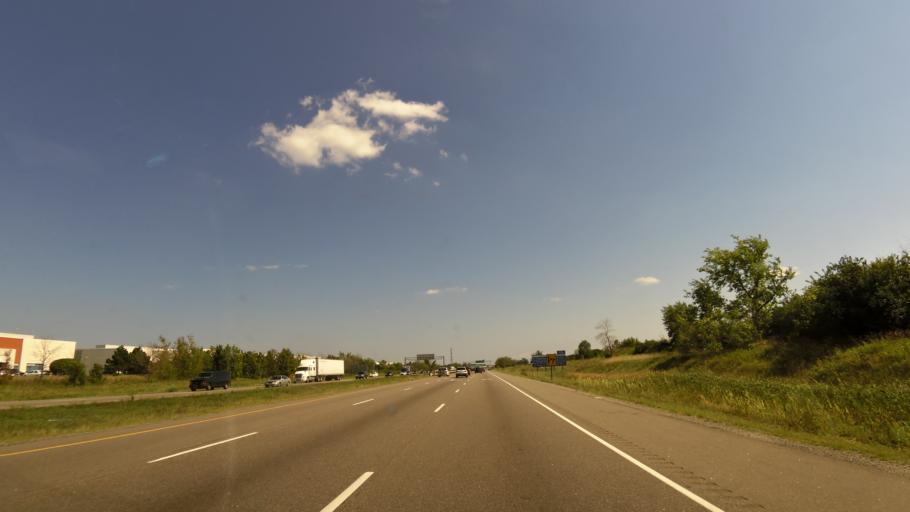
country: CA
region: Ontario
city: Oakville
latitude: 43.5191
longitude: -79.7078
